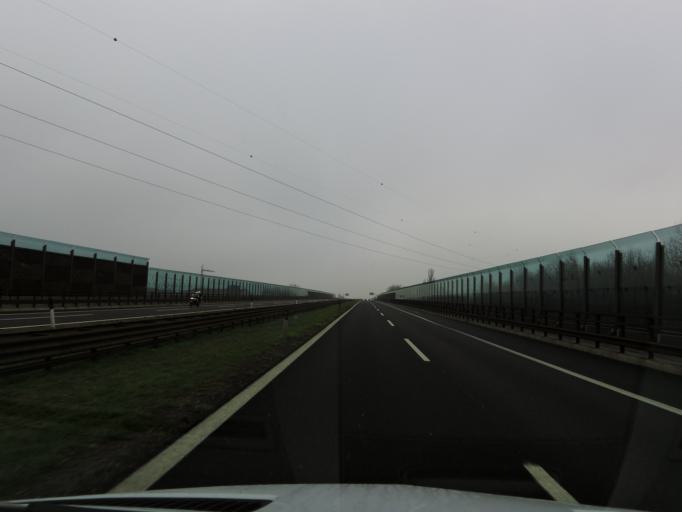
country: IT
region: Lombardy
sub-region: Provincia di Mantova
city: Pegognaga
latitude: 44.9966
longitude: 10.8505
